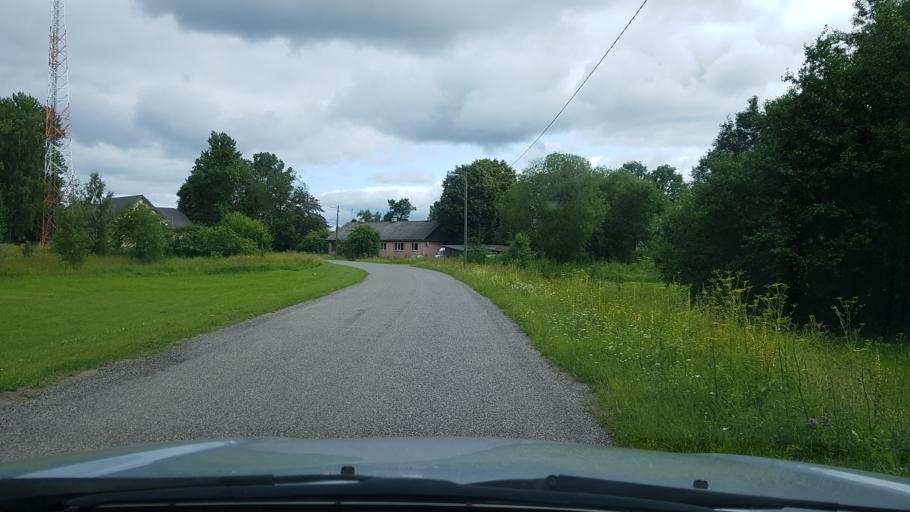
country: EE
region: Ida-Virumaa
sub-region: Sillamaee linn
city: Sillamae
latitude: 59.3714
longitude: 27.7661
